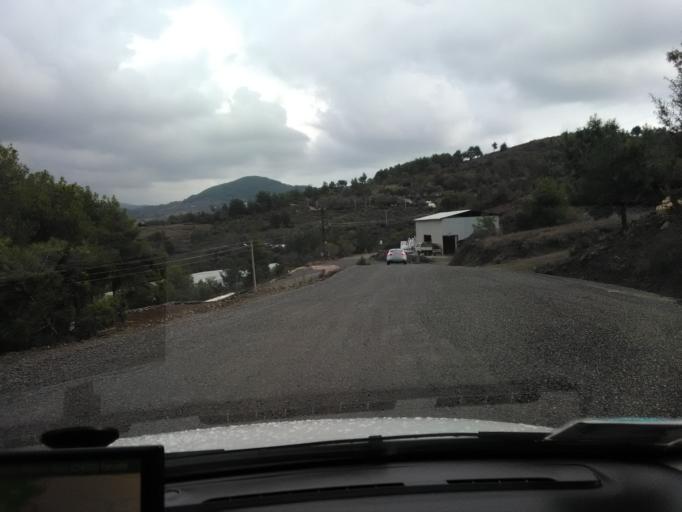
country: TR
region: Antalya
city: Gazipasa
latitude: 36.1604
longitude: 32.4316
